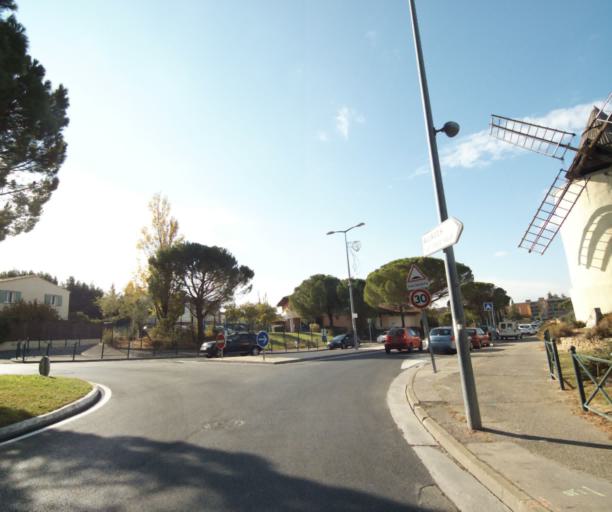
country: FR
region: Provence-Alpes-Cote d'Azur
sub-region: Departement des Bouches-du-Rhone
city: Plan-de-Cuques
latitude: 43.3477
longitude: 5.4680
